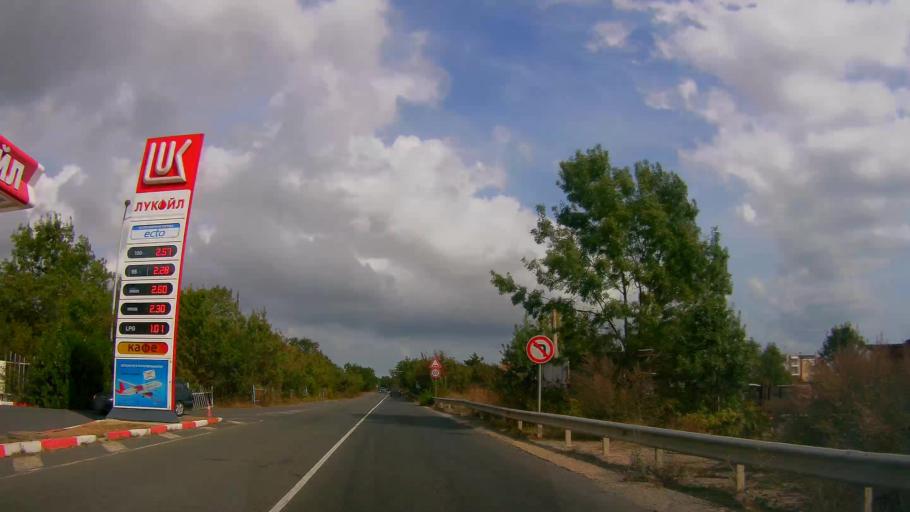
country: BG
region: Burgas
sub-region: Obshtina Primorsko
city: Primorsko
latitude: 42.2685
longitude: 27.7425
